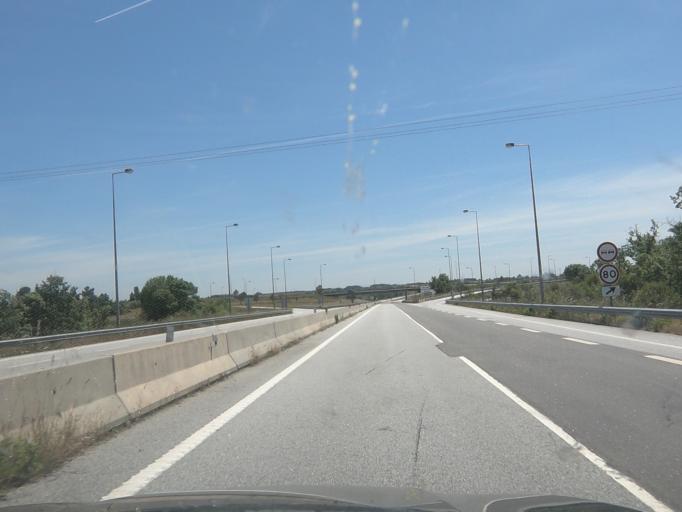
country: ES
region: Castille and Leon
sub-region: Provincia de Salamanca
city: Fuentes de Onoro
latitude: 40.6080
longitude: -6.9868
